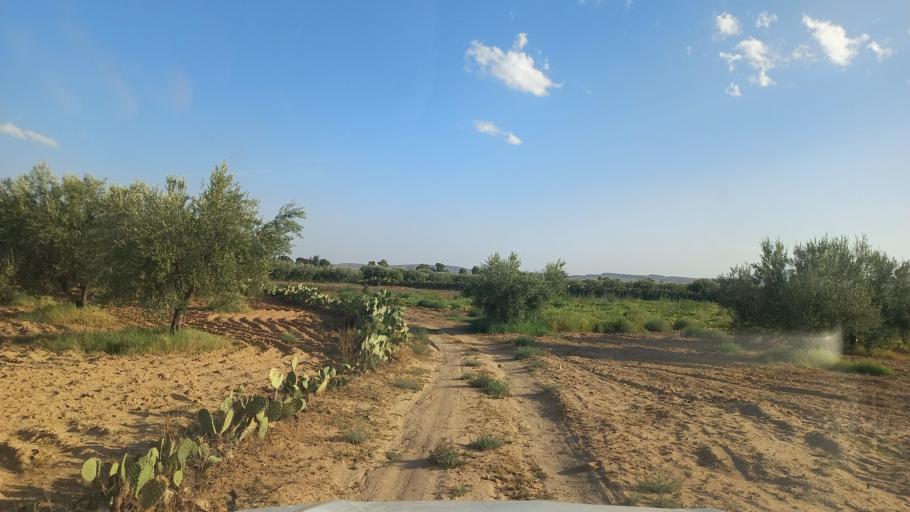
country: TN
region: Al Qasrayn
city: Kasserine
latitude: 35.2662
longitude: 9.0328
